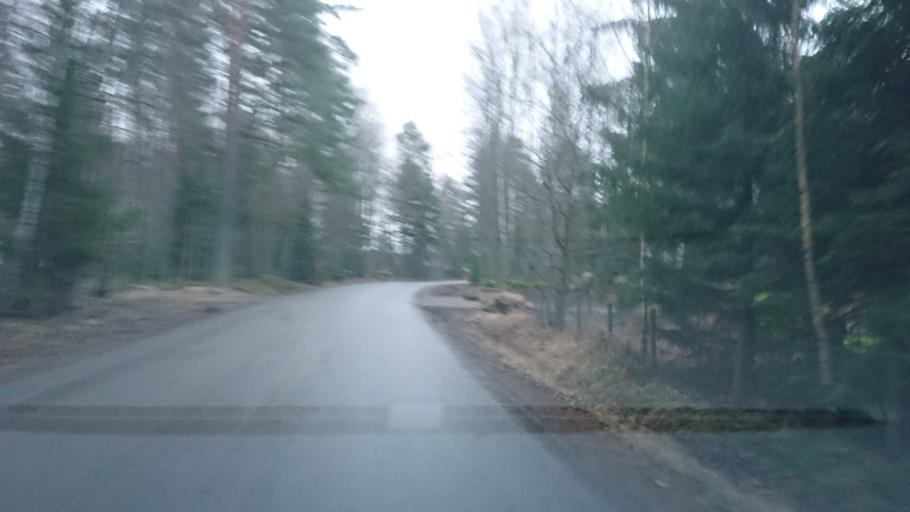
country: SE
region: Uppsala
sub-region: Osthammars Kommun
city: Bjorklinge
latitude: 59.9788
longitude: 17.5955
